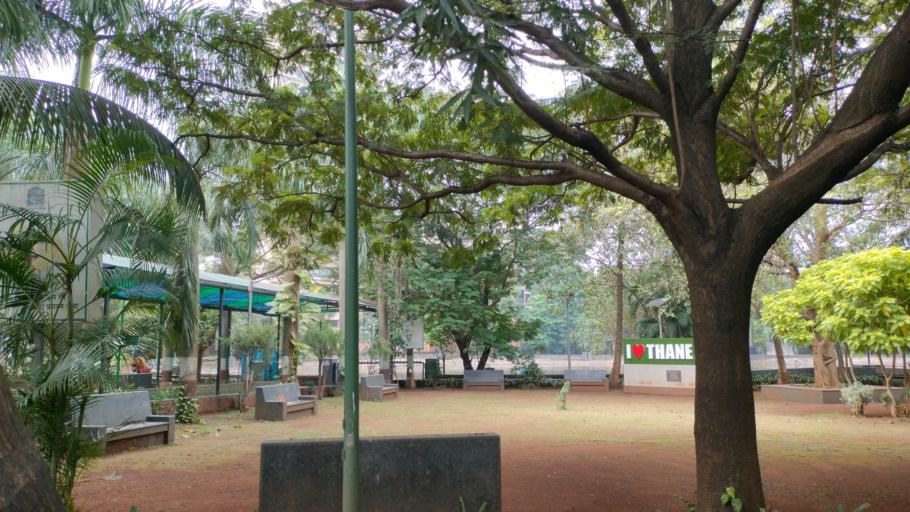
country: IN
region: Maharashtra
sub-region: Thane
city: Thane
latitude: 19.2021
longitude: 72.9753
